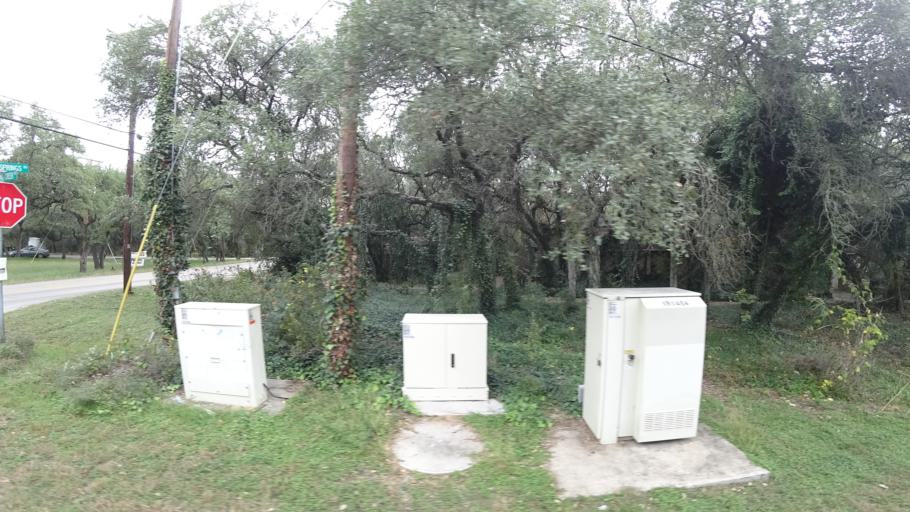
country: US
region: Texas
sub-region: Travis County
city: Barton Creek
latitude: 30.2520
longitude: -97.9189
